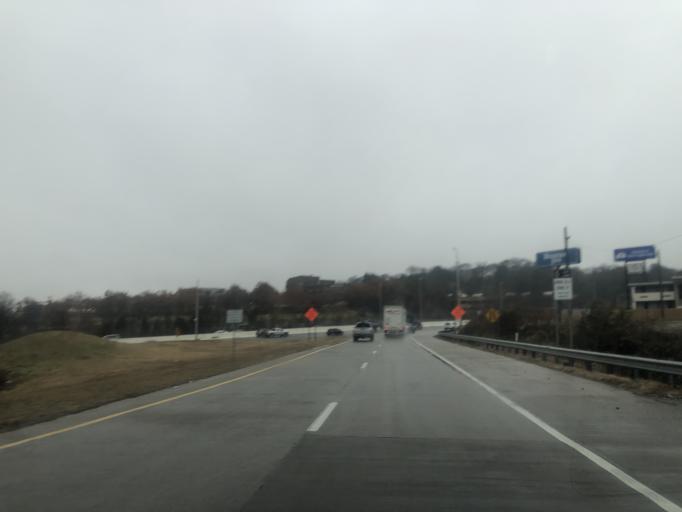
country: US
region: Tennessee
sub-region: Davidson County
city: Oak Hill
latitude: 36.0853
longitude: -86.7012
